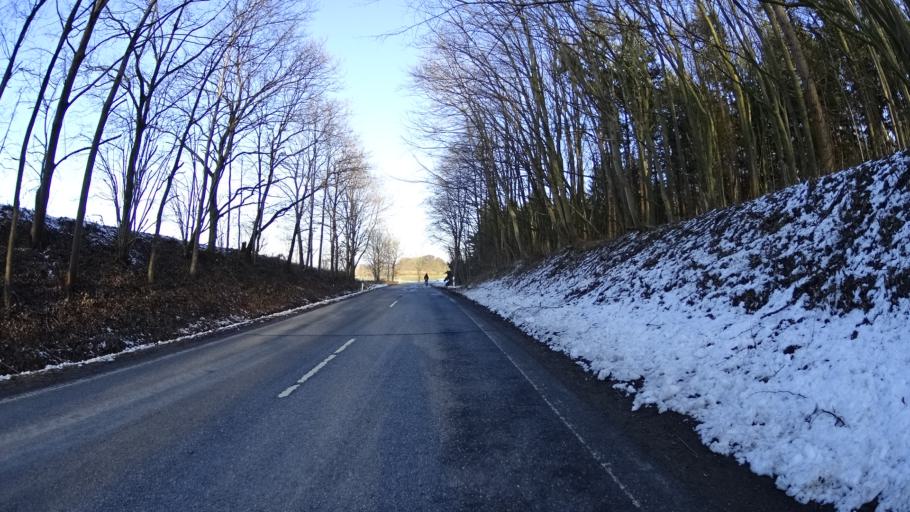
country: DE
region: Schleswig-Holstein
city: Fargau-Pratjau
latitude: 54.3223
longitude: 10.4008
